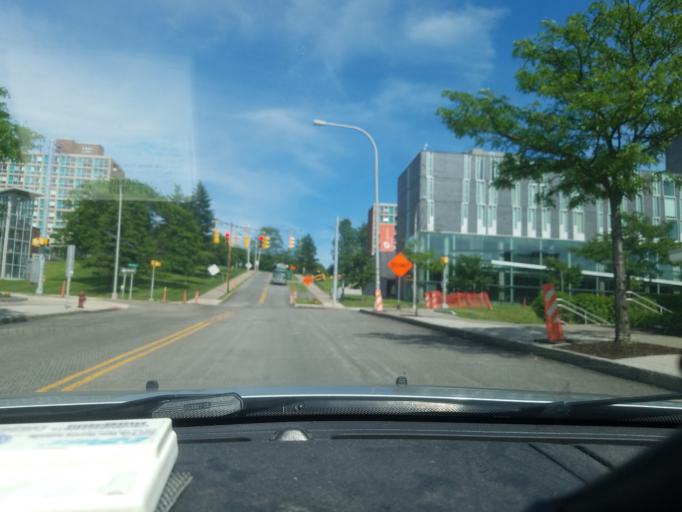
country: US
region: New York
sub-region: Onondaga County
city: Syracuse
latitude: 43.0404
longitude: -76.1306
